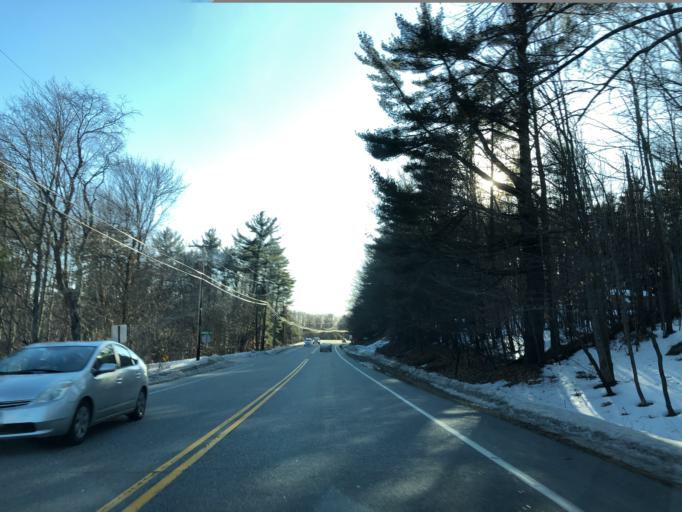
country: US
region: Maine
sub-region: Cumberland County
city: North Windham
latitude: 43.8625
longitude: -70.3711
